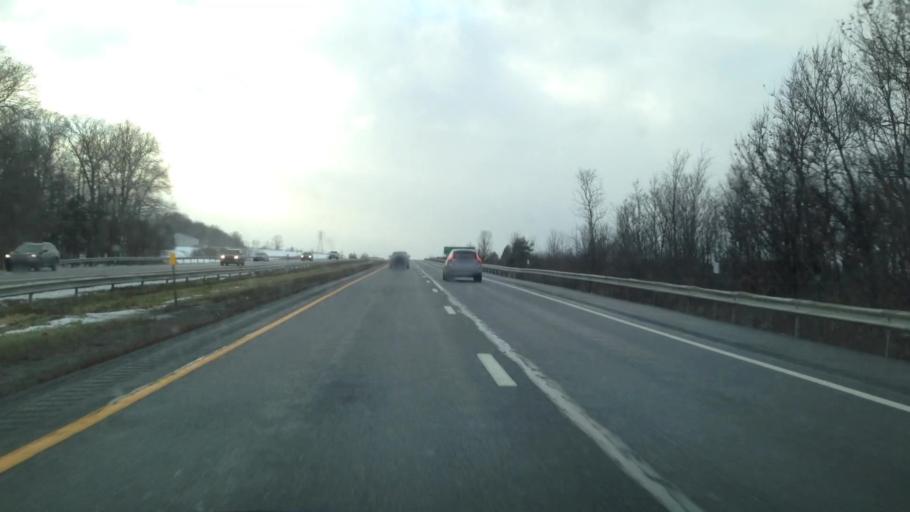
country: US
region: New York
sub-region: Montgomery County
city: Amsterdam
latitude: 42.9178
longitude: -74.1723
